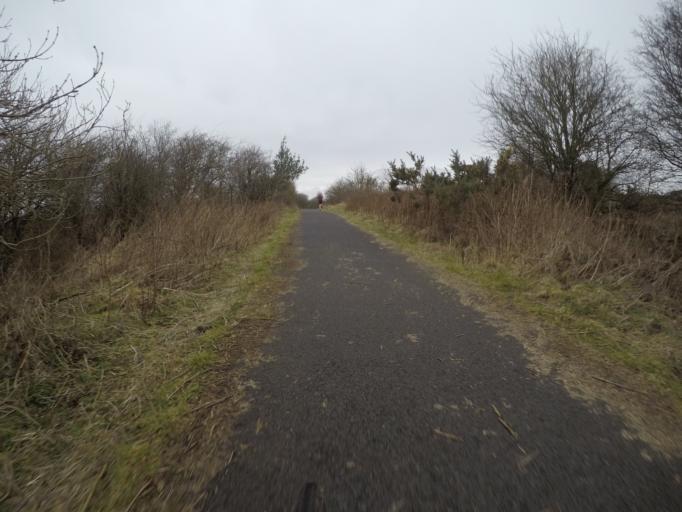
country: GB
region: Scotland
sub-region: North Ayrshire
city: Kilwinning
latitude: 55.6286
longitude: -4.6869
